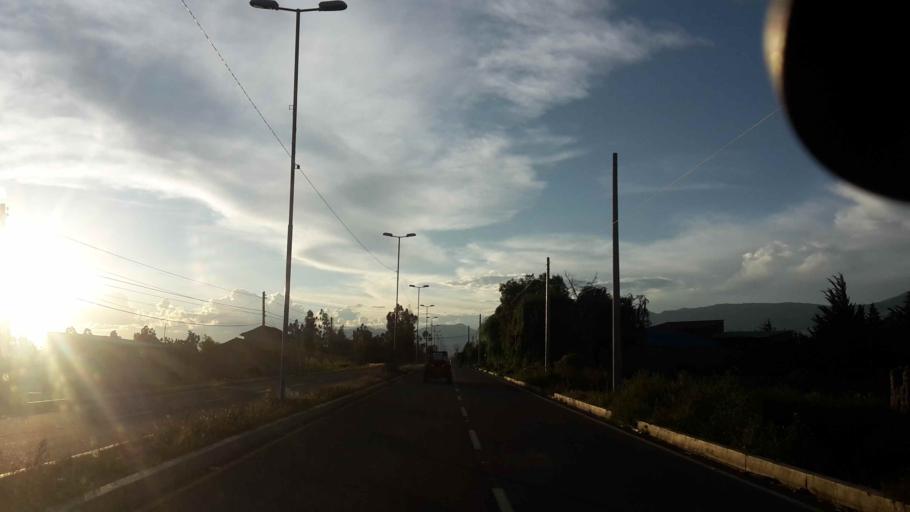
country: BO
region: Cochabamba
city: Arani
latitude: -17.5630
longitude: -65.7935
